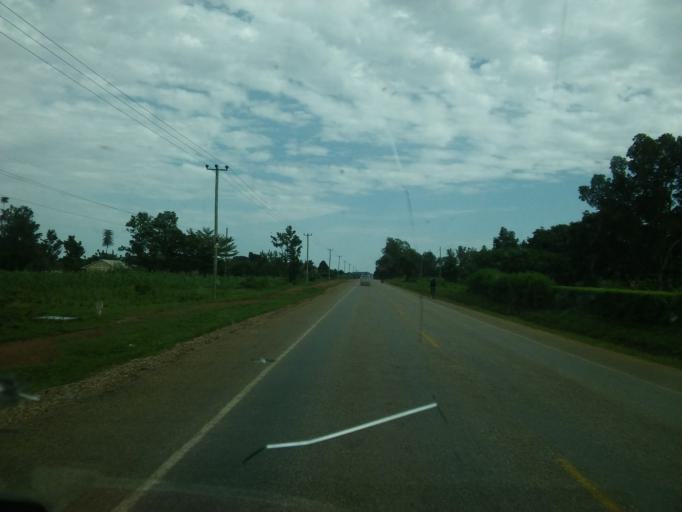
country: UG
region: Eastern Region
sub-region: Mbale District
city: Mbale
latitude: 1.1879
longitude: 34.1400
